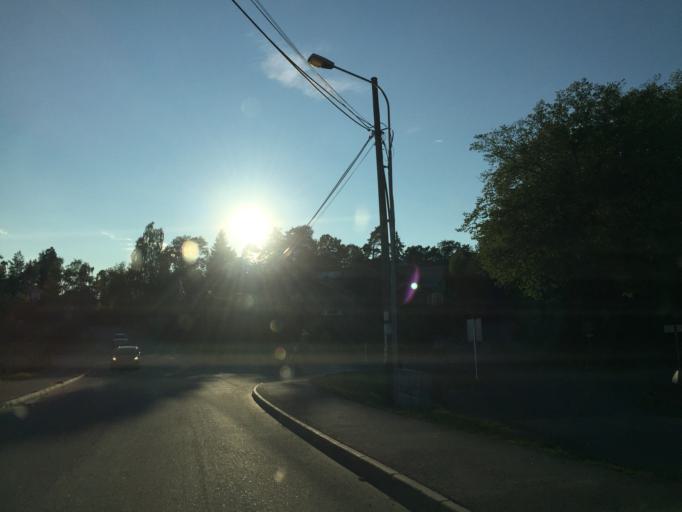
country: NO
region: Akershus
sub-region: Baerum
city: Lysaker
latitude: 59.9033
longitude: 10.6041
